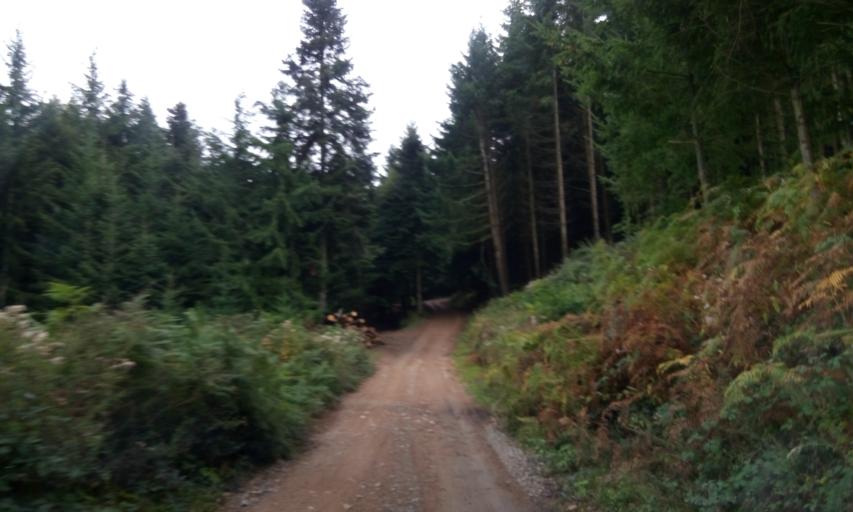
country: FR
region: Rhone-Alpes
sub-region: Departement du Rhone
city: Cublize
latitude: 46.0246
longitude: 4.4262
